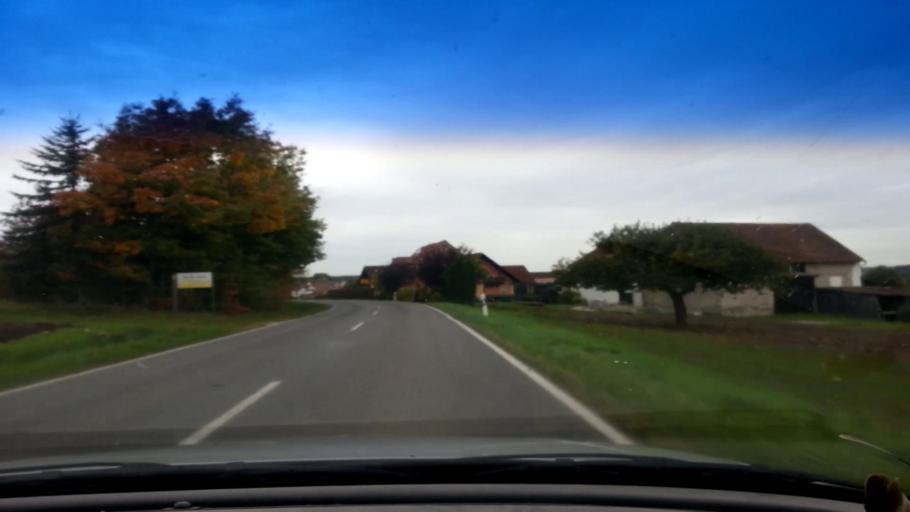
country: DE
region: Bavaria
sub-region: Upper Franconia
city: Priesendorf
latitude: 49.9041
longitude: 10.6800
